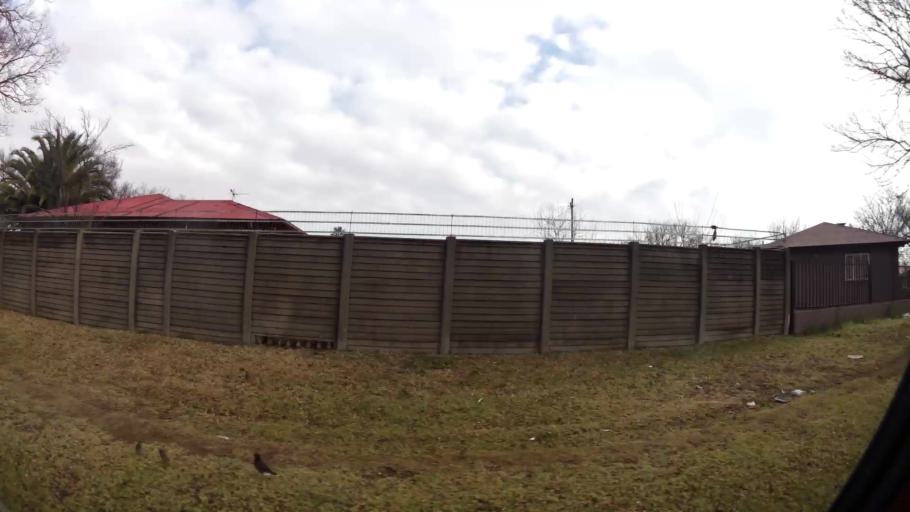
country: ZA
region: Gauteng
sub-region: Sedibeng District Municipality
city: Vanderbijlpark
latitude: -26.6910
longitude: 27.8206
